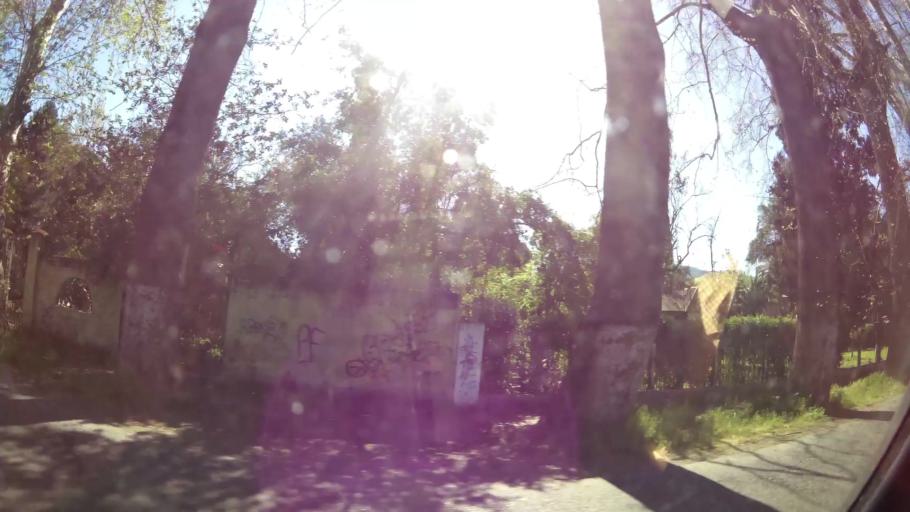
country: CL
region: Santiago Metropolitan
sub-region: Provincia de Talagante
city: Penaflor
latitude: -33.6020
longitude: -70.8969
